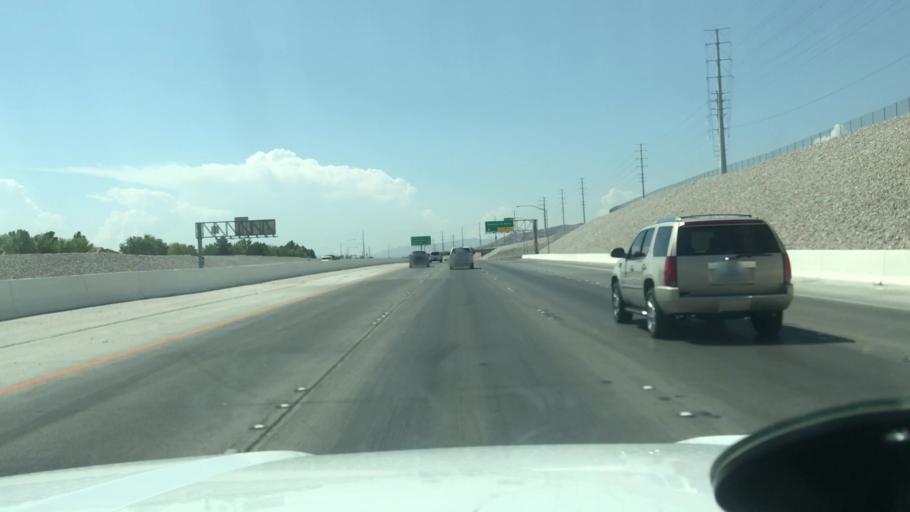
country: US
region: Nevada
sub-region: Clark County
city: Summerlin South
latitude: 36.1985
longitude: -115.3418
